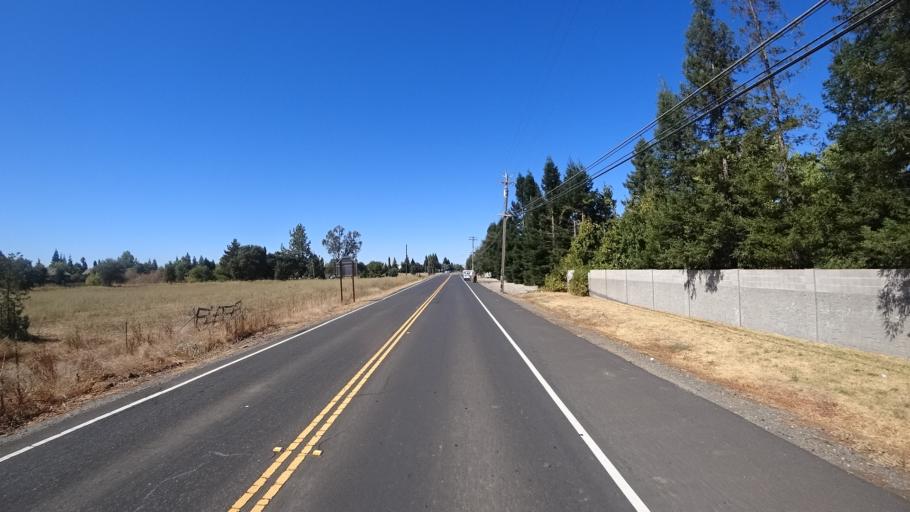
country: US
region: California
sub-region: Sacramento County
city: Elk Grove
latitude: 38.4237
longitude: -121.3309
